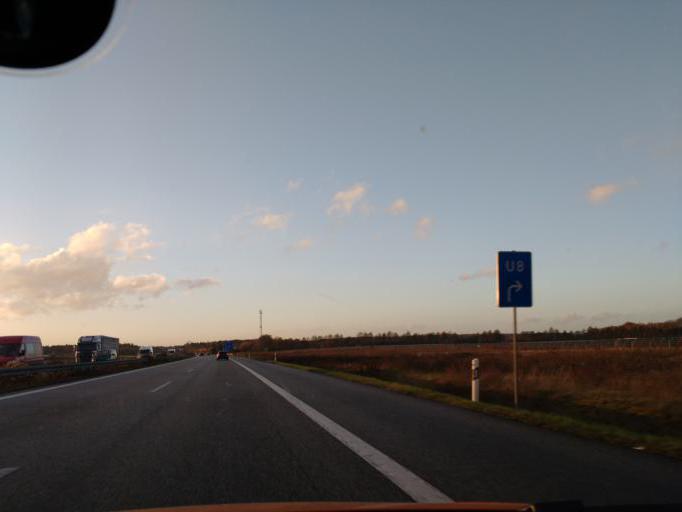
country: DE
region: Mecklenburg-Vorpommern
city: Sulstorf
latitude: 53.4826
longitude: 11.2846
